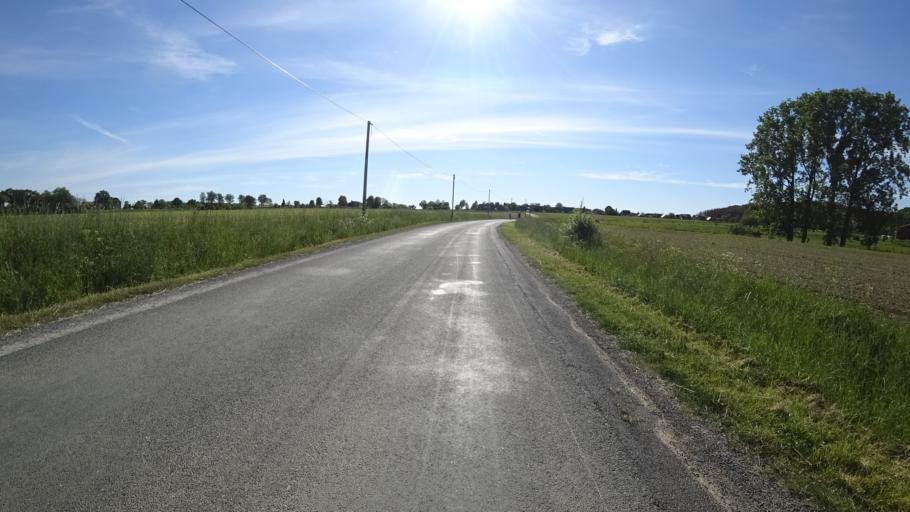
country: DE
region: North Rhine-Westphalia
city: Oelde
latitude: 51.7690
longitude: 8.1684
